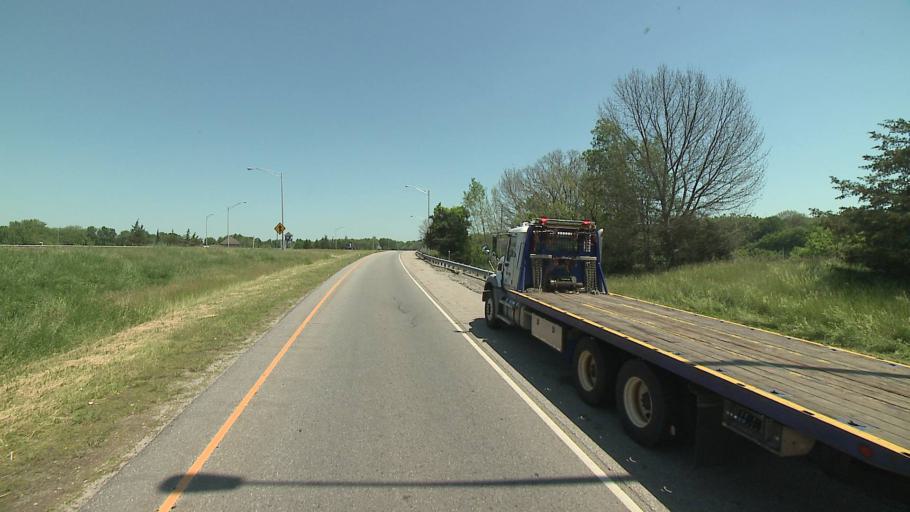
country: US
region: Connecticut
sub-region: Windham County
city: Plainfield
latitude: 41.6655
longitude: -71.9133
